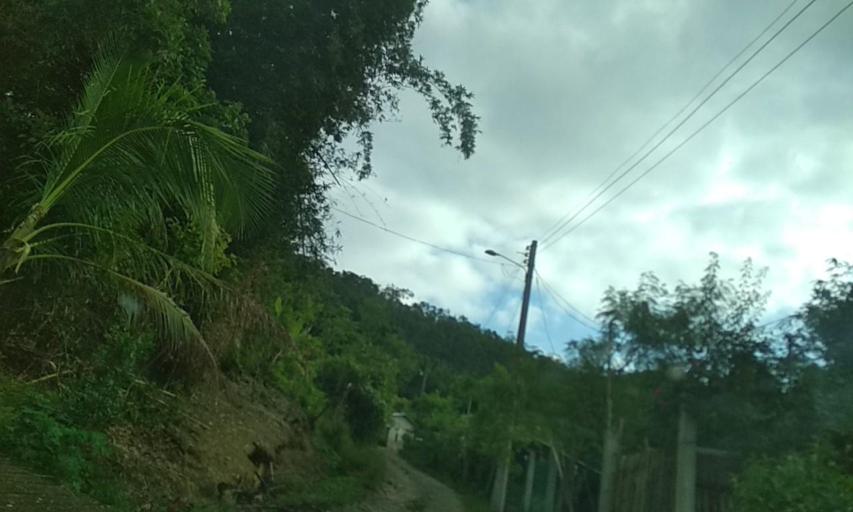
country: MX
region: Veracruz
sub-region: Papantla
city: Polutla
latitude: 20.5727
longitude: -97.2521
